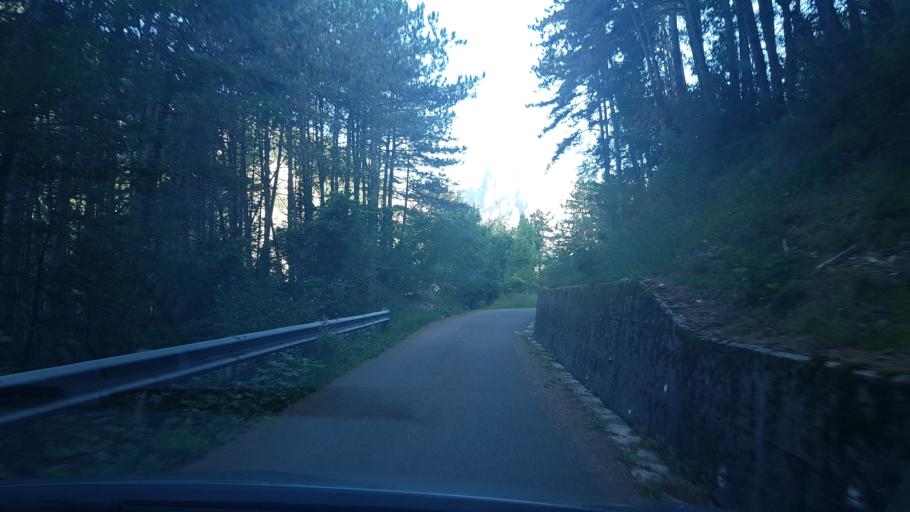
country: IT
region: Friuli Venezia Giulia
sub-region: Provincia di Udine
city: Moggio Udinese
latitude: 46.4324
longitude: 13.2045
